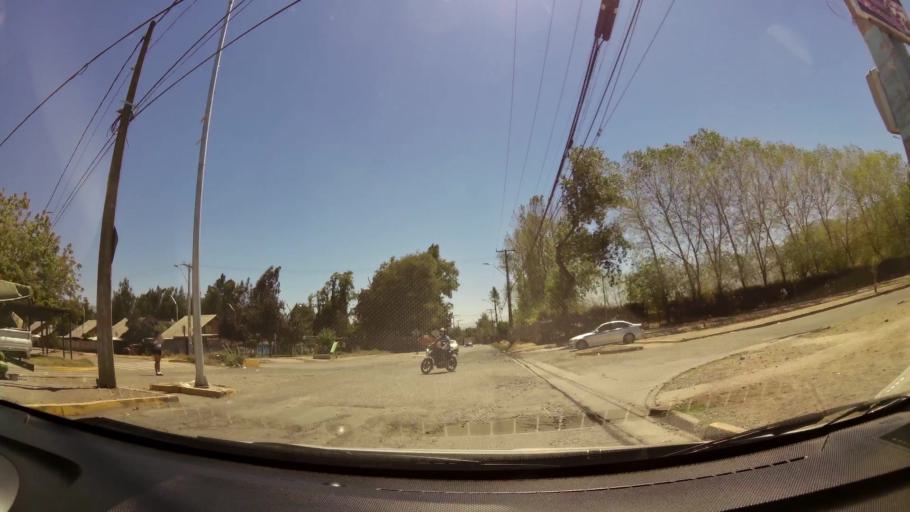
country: CL
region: O'Higgins
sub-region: Provincia de Cachapoal
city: Rancagua
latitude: -34.1493
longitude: -70.7231
